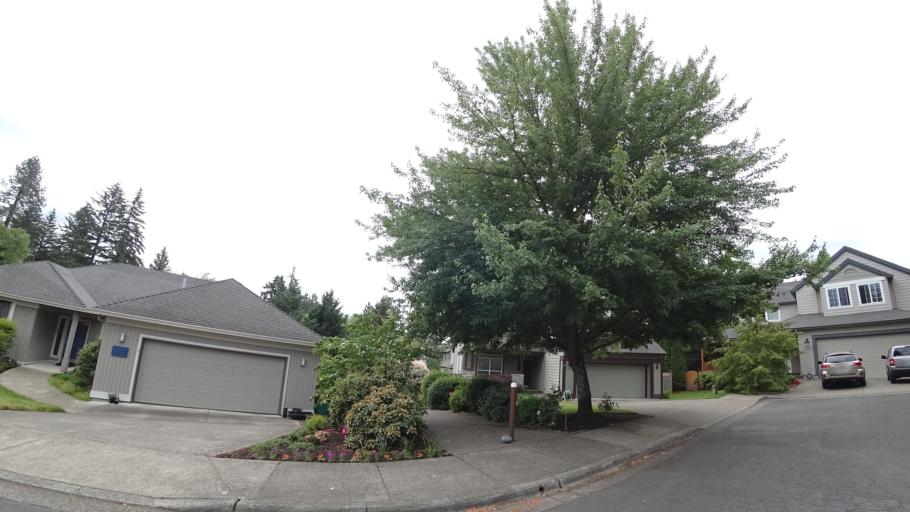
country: US
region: Oregon
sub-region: Washington County
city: Metzger
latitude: 45.4535
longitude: -122.7625
